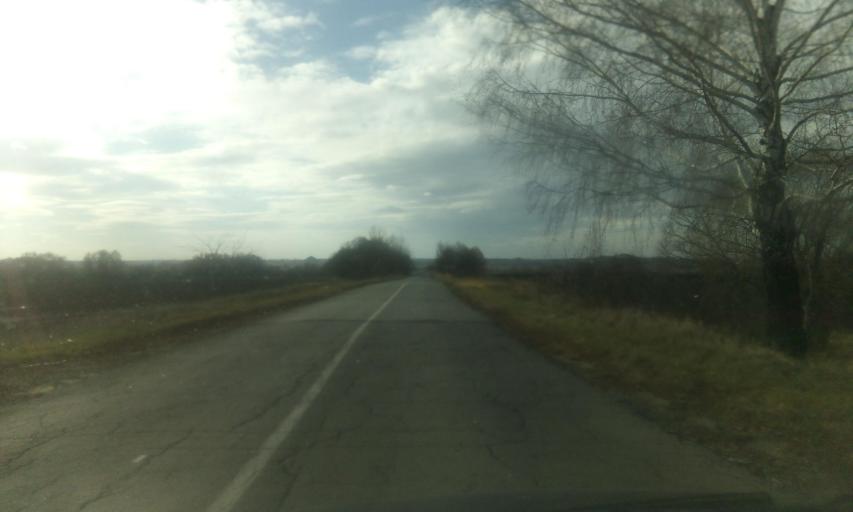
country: RU
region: Tula
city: Dubovka
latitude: 53.9556
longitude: 38.0366
